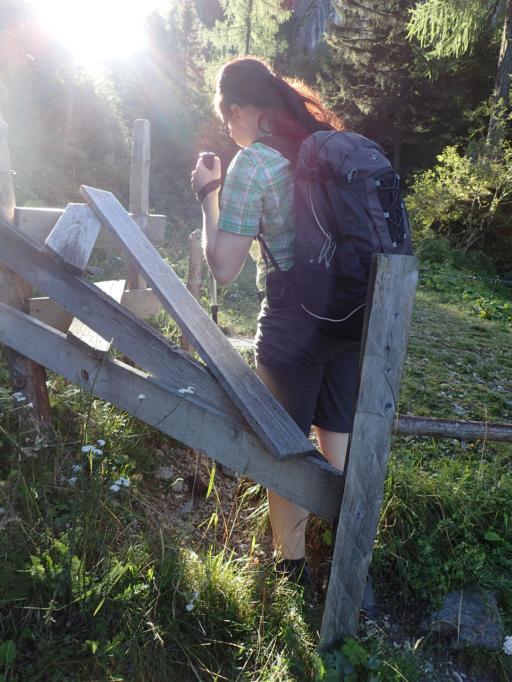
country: AT
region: Salzburg
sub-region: Politischer Bezirk Sankt Johann im Pongau
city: Untertauern
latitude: 47.2504
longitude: 13.5084
